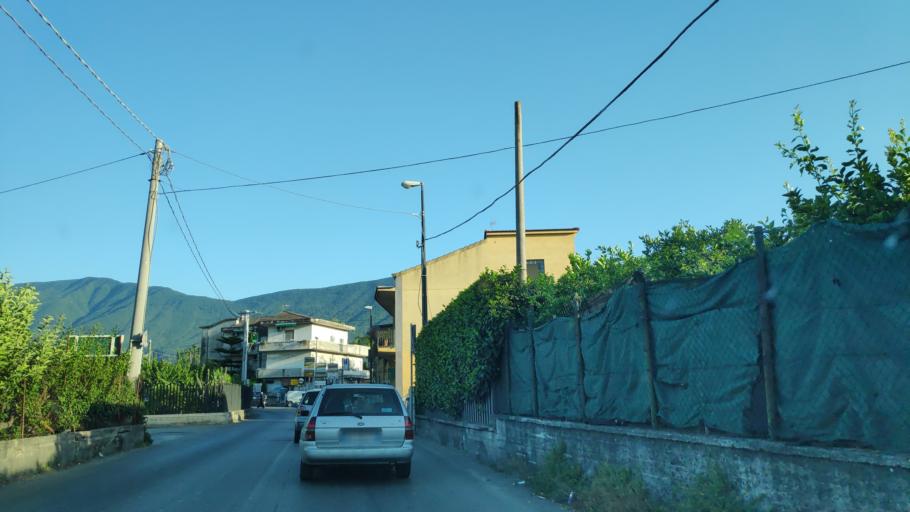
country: IT
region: Campania
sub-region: Provincia di Salerno
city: Pagani
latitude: 40.7625
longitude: 14.6154
